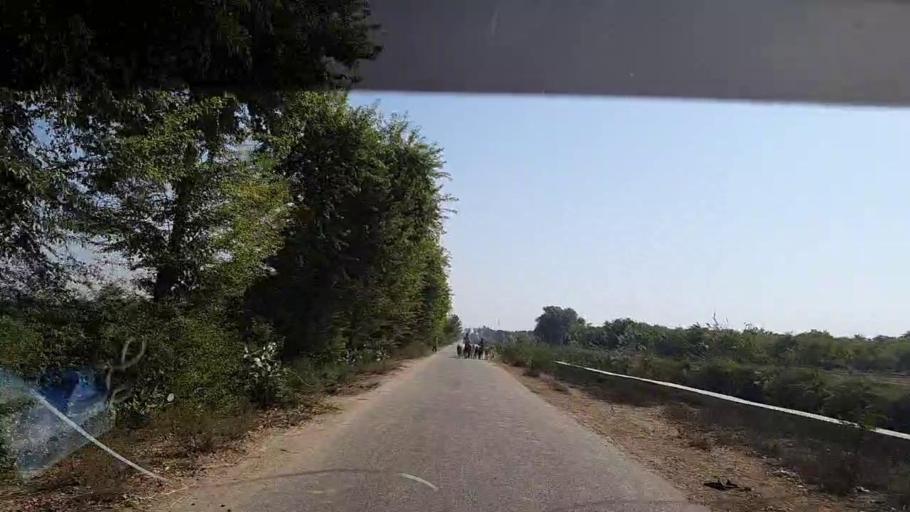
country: PK
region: Sindh
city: Larkana
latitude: 27.6042
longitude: 68.2607
